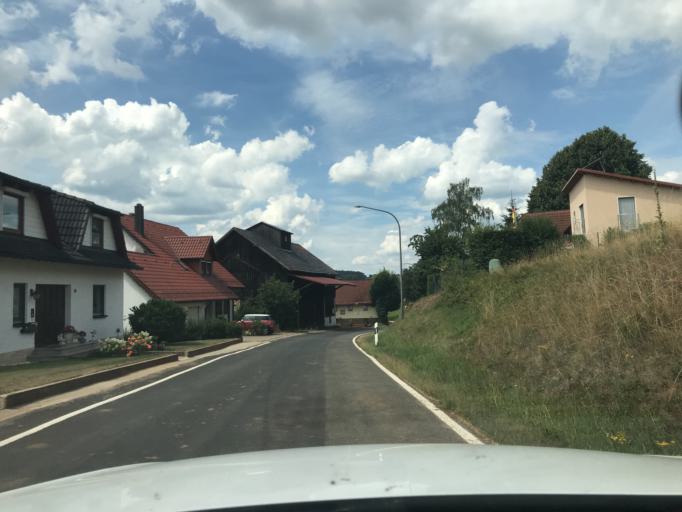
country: DE
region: Bavaria
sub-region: Upper Palatinate
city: Auerbach
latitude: 49.7467
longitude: 11.6215
